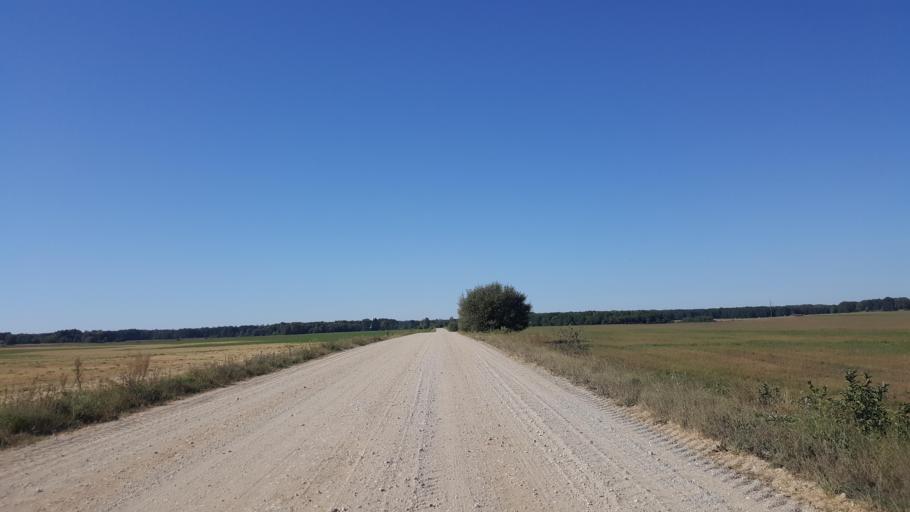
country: BY
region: Brest
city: Charnawchytsy
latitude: 52.3330
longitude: 23.6265
